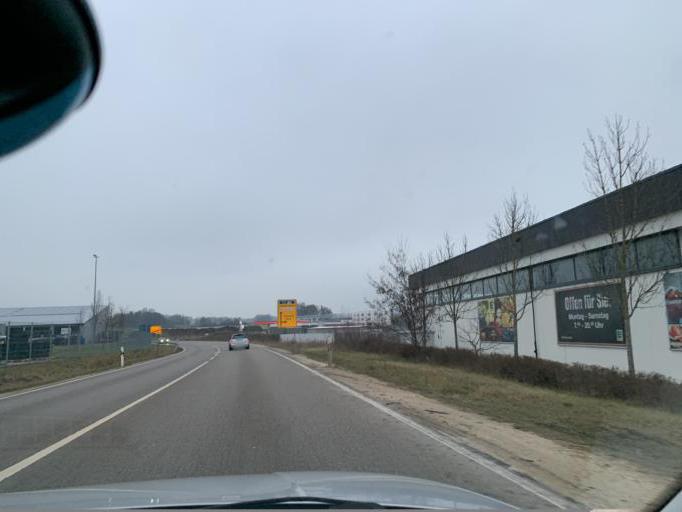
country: DE
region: Bavaria
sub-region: Upper Bavaria
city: Hepberg
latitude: 48.8091
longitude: 11.4804
